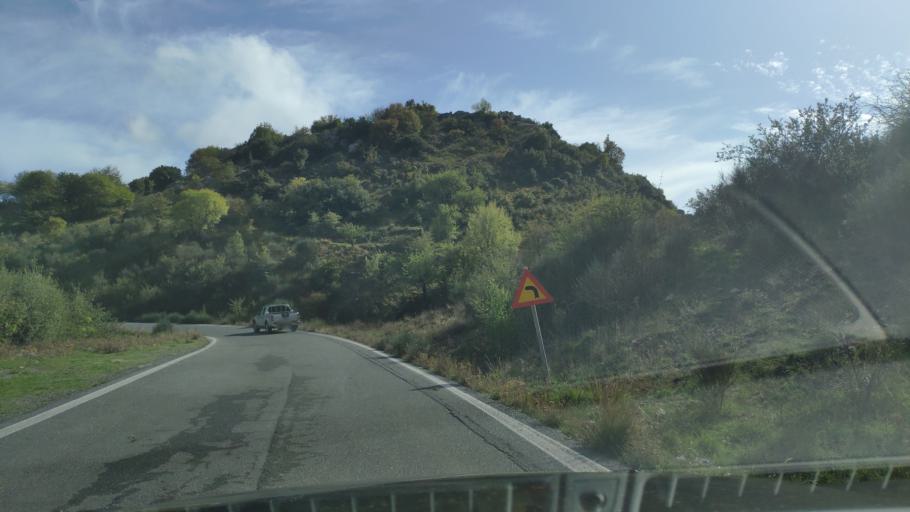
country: GR
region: Peloponnese
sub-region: Nomos Arkadias
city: Dimitsana
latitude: 37.5794
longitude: 22.0163
